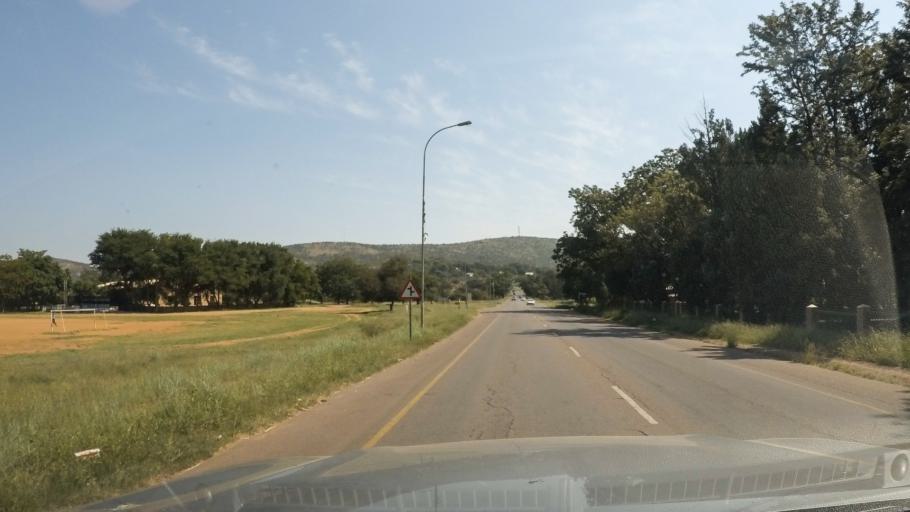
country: BW
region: South East
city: Lobatse
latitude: -25.2280
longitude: 25.6808
